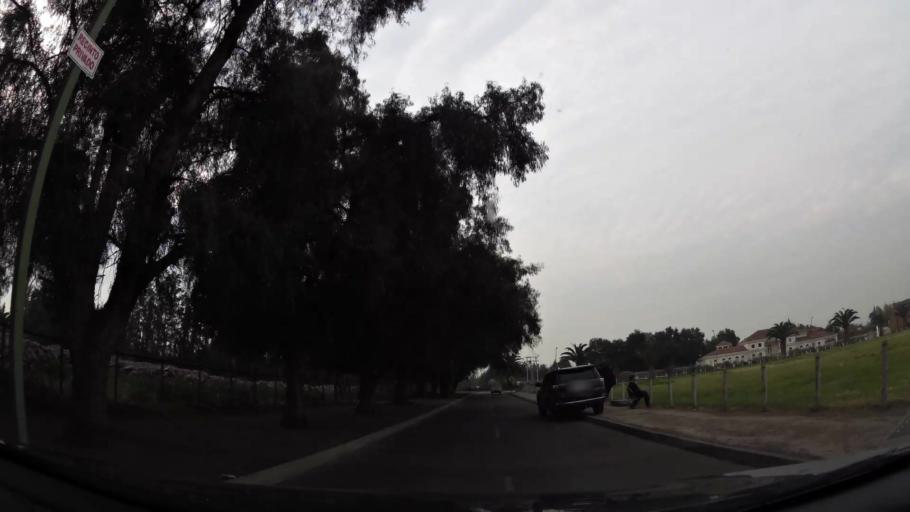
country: CL
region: Santiago Metropolitan
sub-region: Provincia de Chacabuco
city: Chicureo Abajo
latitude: -33.2773
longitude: -70.7051
